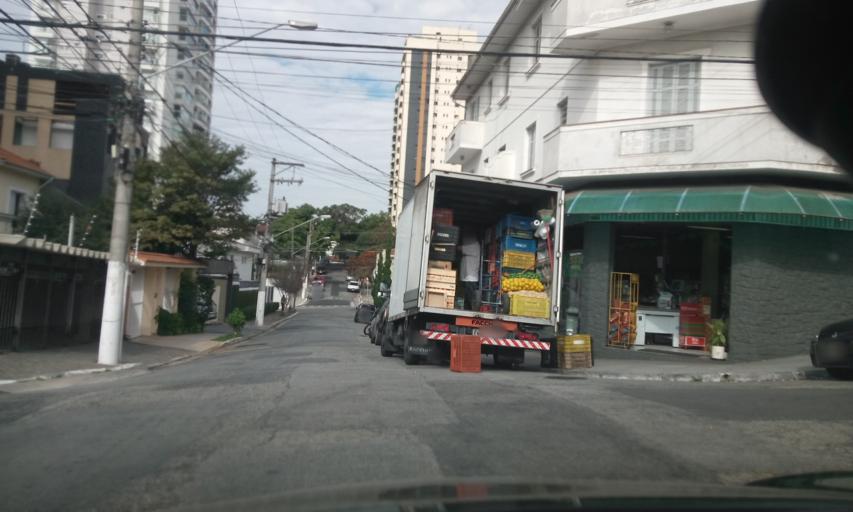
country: BR
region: Sao Paulo
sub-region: Sao Paulo
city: Sao Paulo
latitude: -23.5977
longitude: -46.6305
